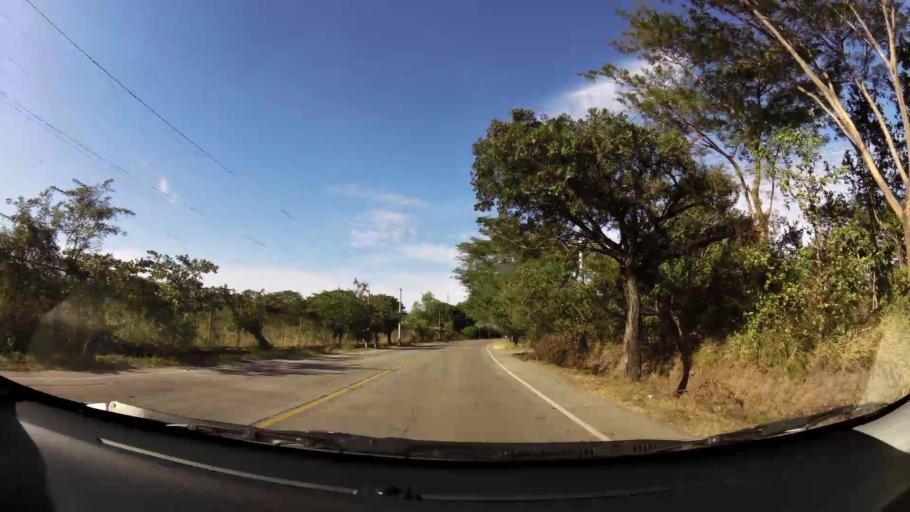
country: SV
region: Santa Ana
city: Texistepeque
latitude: 14.1021
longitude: -89.5000
